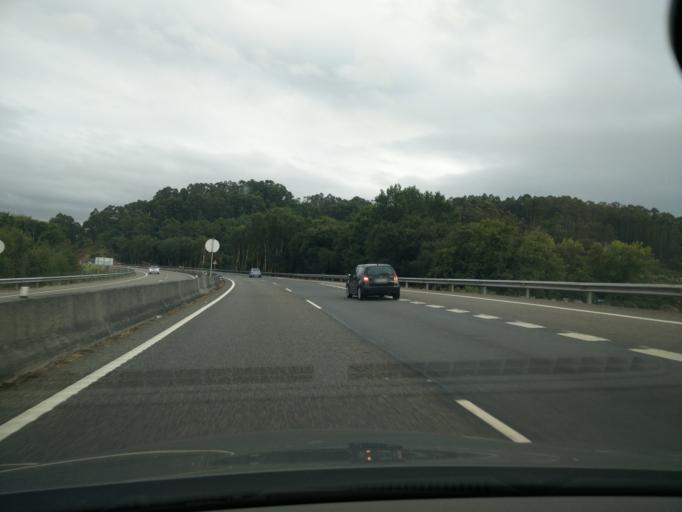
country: ES
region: Galicia
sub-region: Provincia da Coruna
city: Cambre
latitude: 43.3081
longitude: -8.3482
